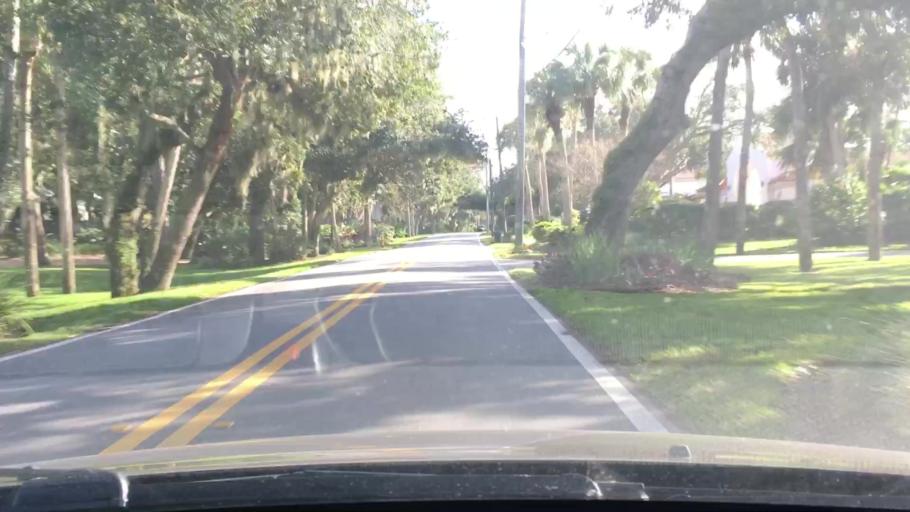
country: US
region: Florida
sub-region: Volusia County
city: Ormond Beach
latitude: 29.3013
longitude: -81.0533
